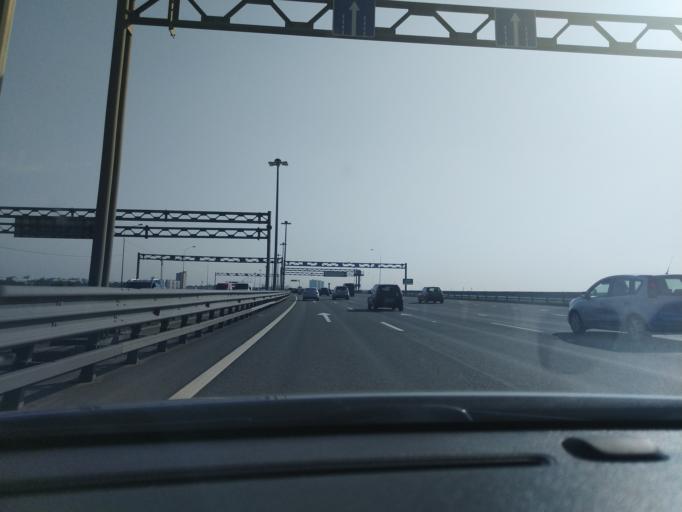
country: RU
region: St.-Petersburg
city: Uritsk
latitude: 59.8150
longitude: 30.2065
